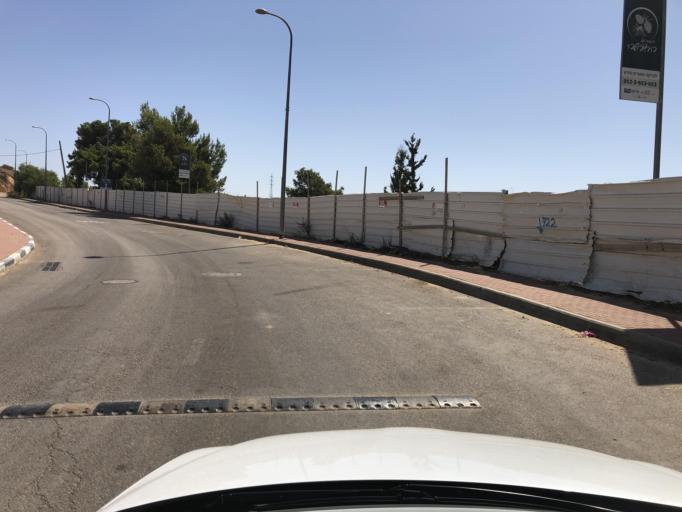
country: PS
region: West Bank
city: An Nabi Ilyas
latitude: 32.1638
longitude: 35.0227
